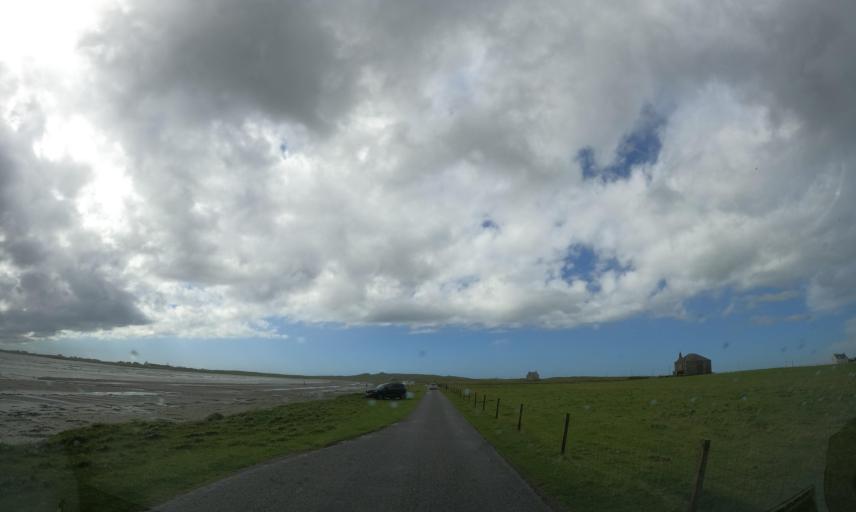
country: GB
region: Scotland
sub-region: Eilean Siar
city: Barra
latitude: 56.5204
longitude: -6.8102
